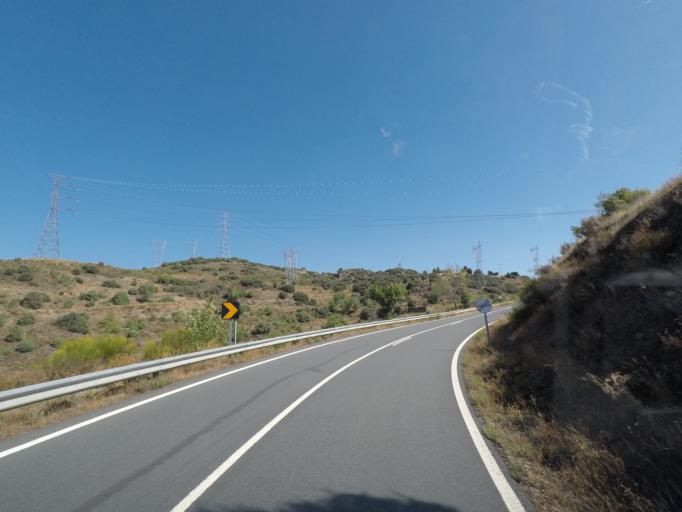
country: ES
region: Castille and Leon
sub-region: Provincia de Salamanca
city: Villarino de los Aires
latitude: 41.3010
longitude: -6.4818
